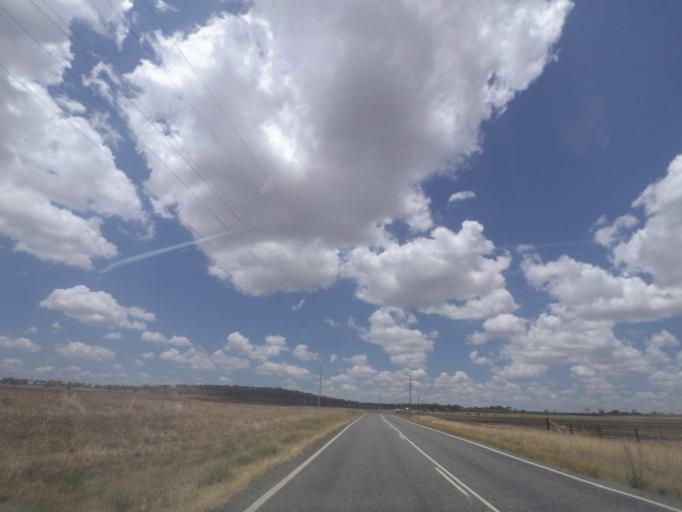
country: AU
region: Queensland
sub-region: Toowoomba
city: Top Camp
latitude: -27.8699
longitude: 151.9597
